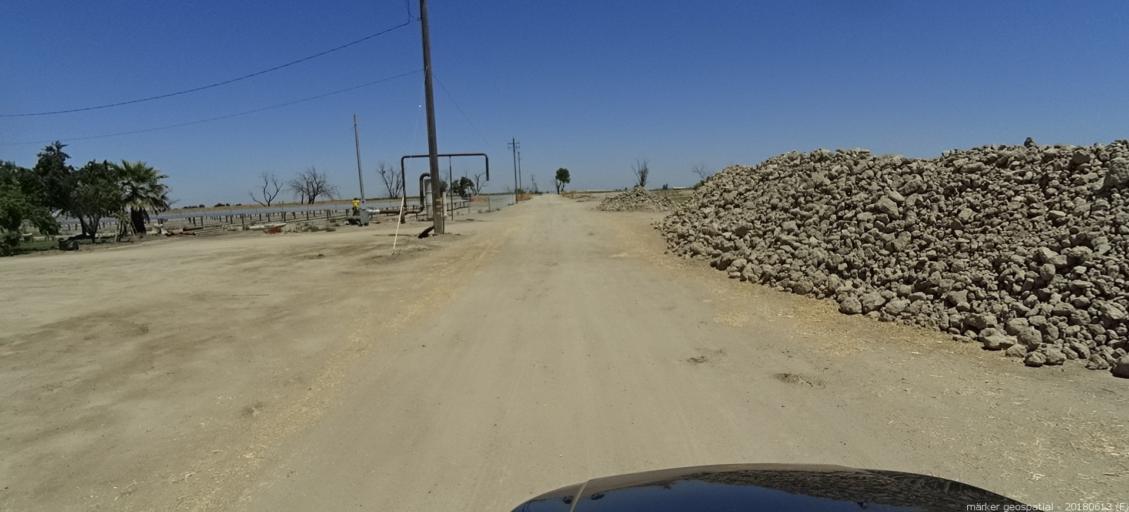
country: US
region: California
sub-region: Madera County
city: Chowchilla
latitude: 36.9942
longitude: -120.3465
